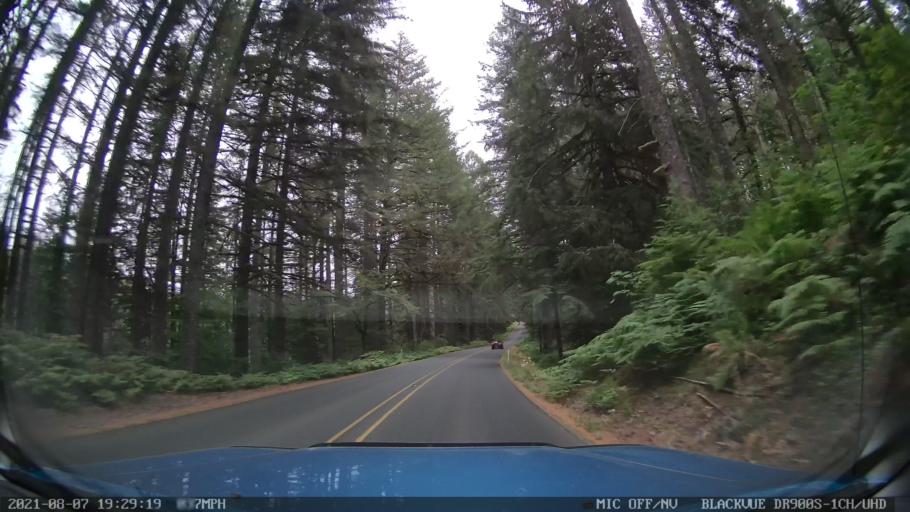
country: US
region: Oregon
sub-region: Linn County
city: Lyons
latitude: 44.8836
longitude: -122.6307
